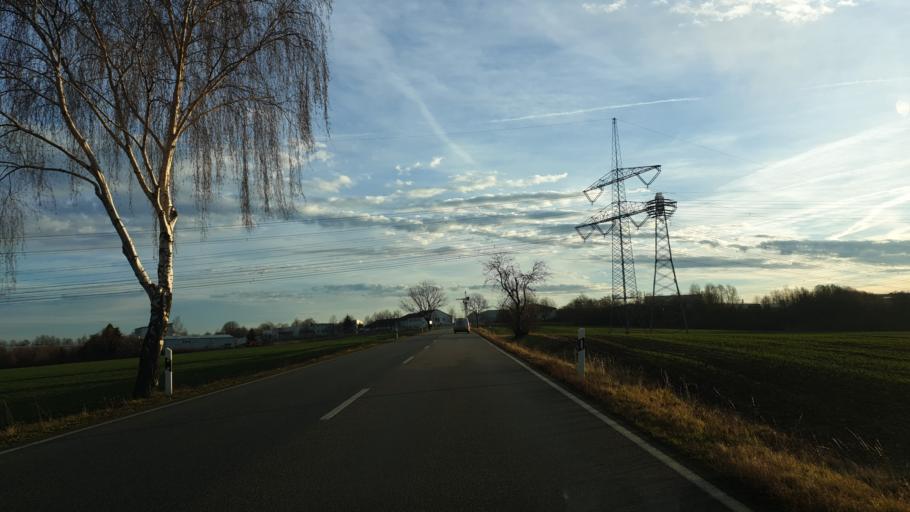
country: DE
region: Saxony
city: Kirchberg
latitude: 50.7916
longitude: 12.7747
